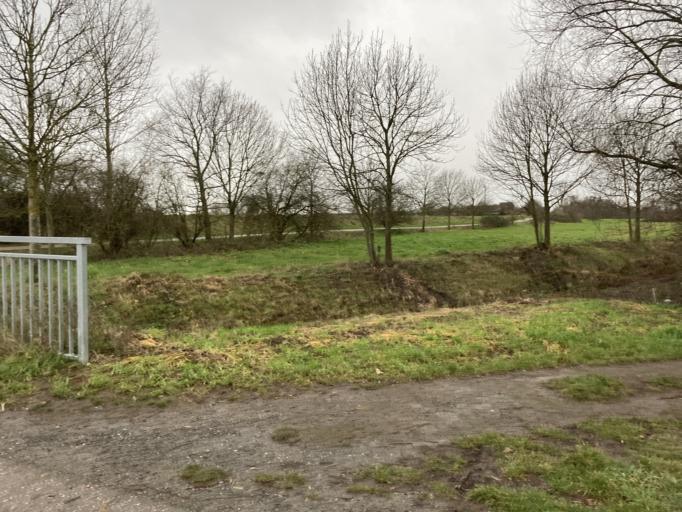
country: DE
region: North Rhine-Westphalia
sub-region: Regierungsbezirk Dusseldorf
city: Meerbusch
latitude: 51.2853
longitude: 6.6917
